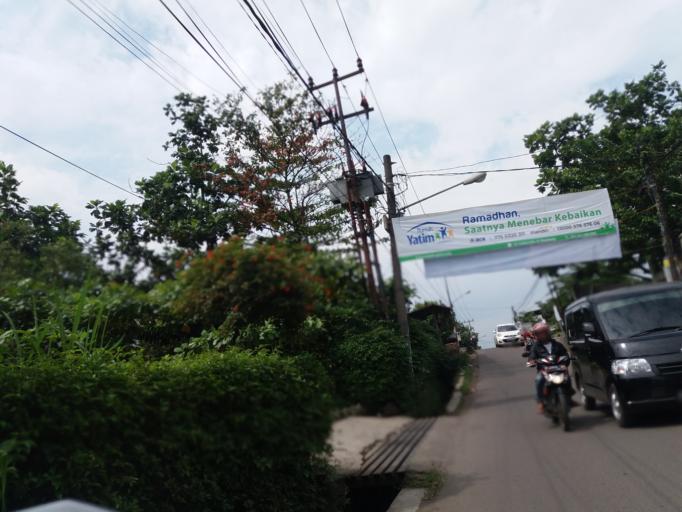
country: ID
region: West Java
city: Bandung
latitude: -6.9276
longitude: 107.6614
